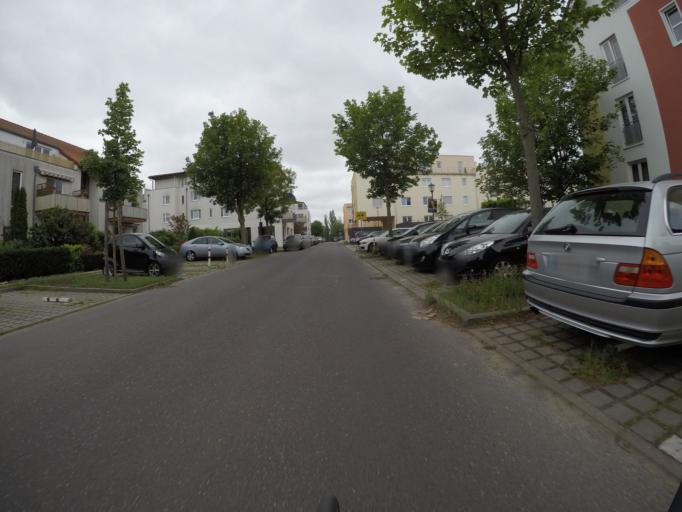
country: DE
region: Brandenburg
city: Glienicke
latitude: 52.6338
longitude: 13.3199
